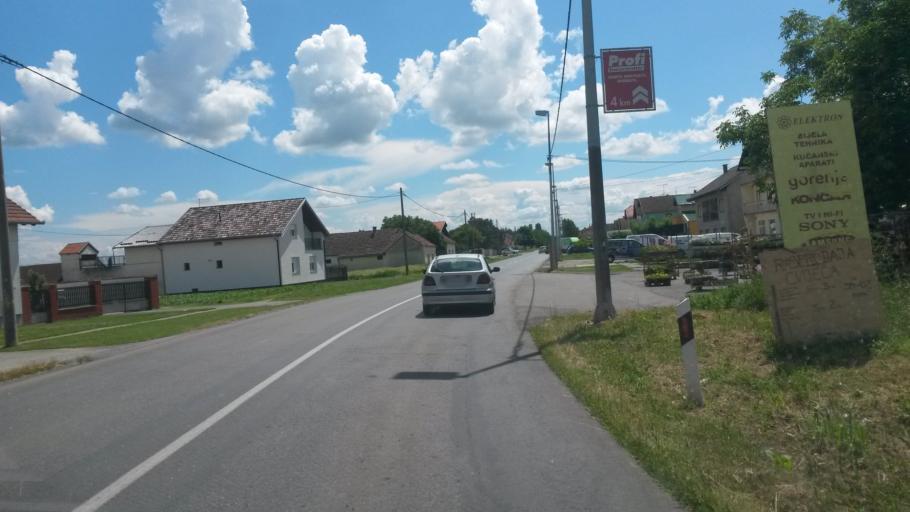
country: HR
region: Osjecko-Baranjska
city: Viskovci
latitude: 45.3342
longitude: 18.4203
